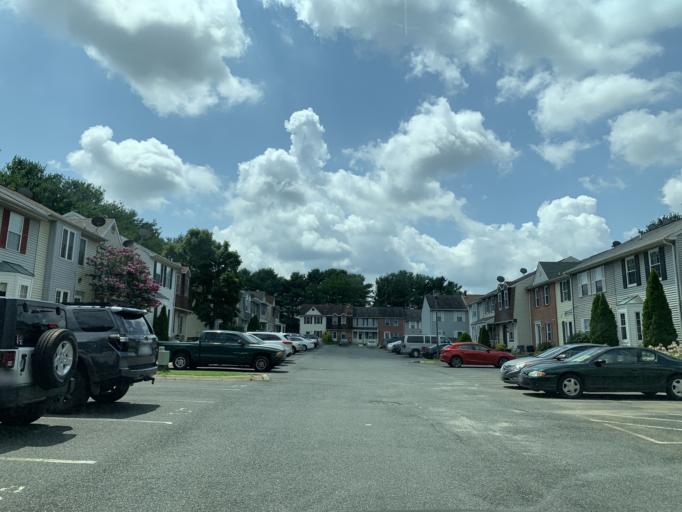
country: US
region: Maryland
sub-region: Harford County
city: Bel Air
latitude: 39.5287
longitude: -76.3551
